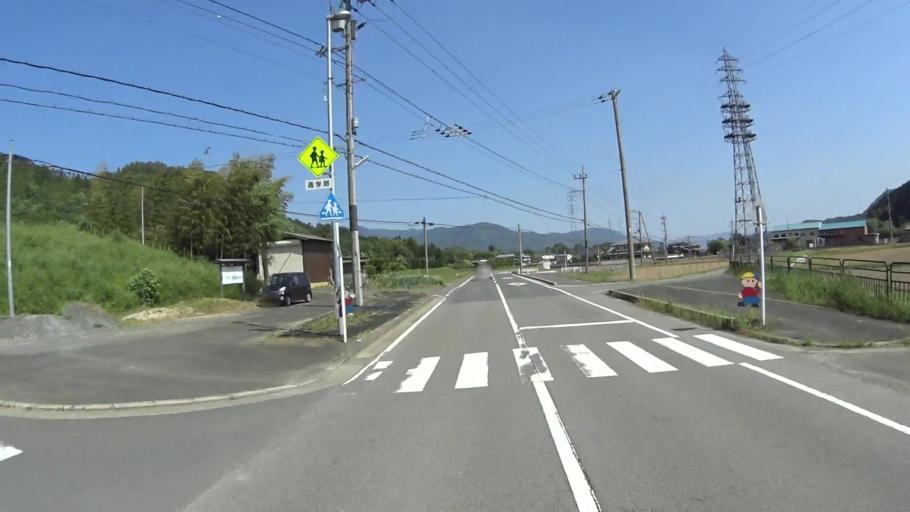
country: JP
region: Kyoto
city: Kameoka
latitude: 35.1069
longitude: 135.5239
